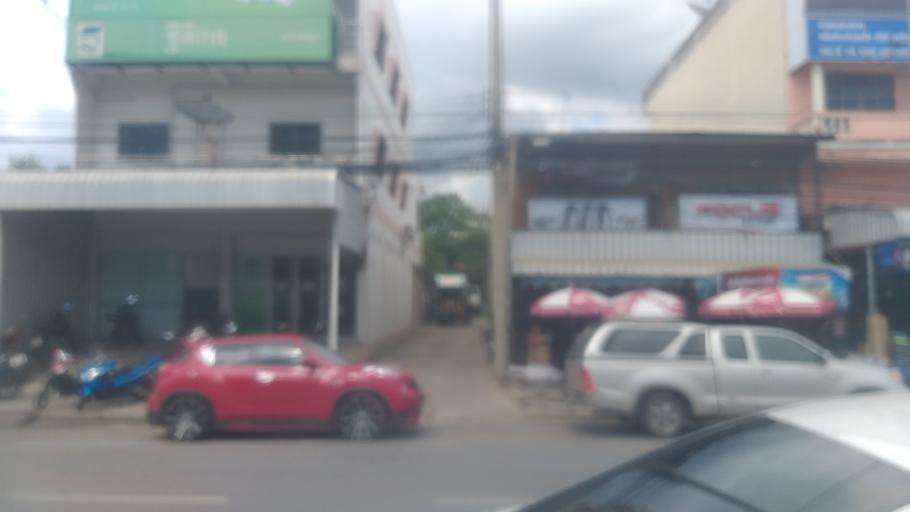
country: TH
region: Chaiyaphum
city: Chaiyaphum
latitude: 15.8014
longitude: 102.0312
